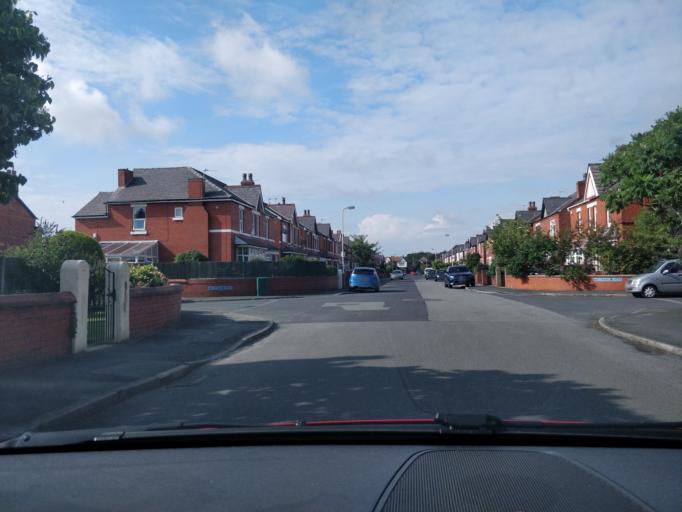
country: GB
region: England
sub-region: Sefton
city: Southport
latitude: 53.6520
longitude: -2.9638
